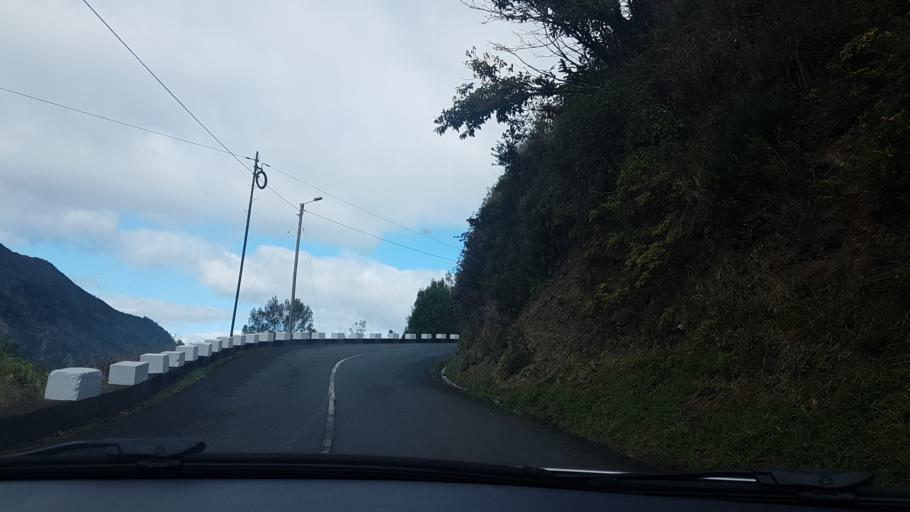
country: PT
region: Madeira
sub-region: Sao Vicente
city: Sao Vicente
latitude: 32.7815
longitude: -17.0304
